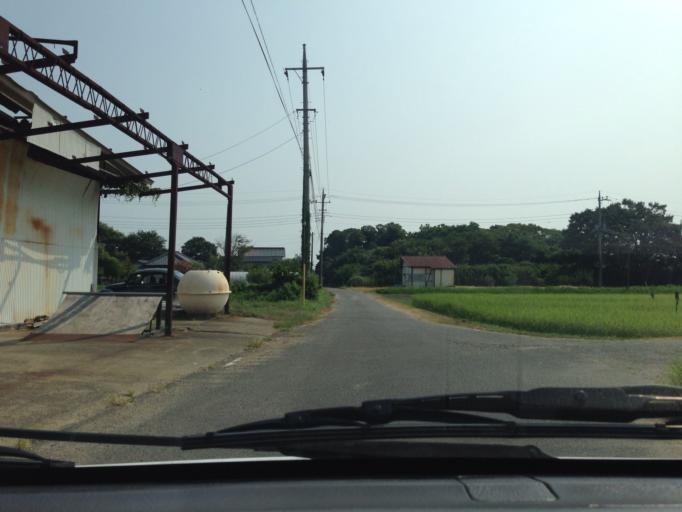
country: JP
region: Ibaraki
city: Inashiki
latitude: 36.0131
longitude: 140.3635
